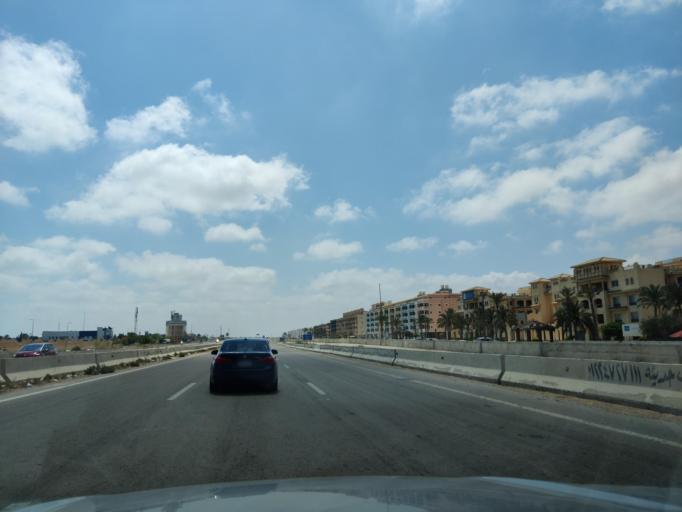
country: EG
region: Muhafazat Matruh
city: Al `Alamayn
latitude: 30.8191
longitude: 29.0224
